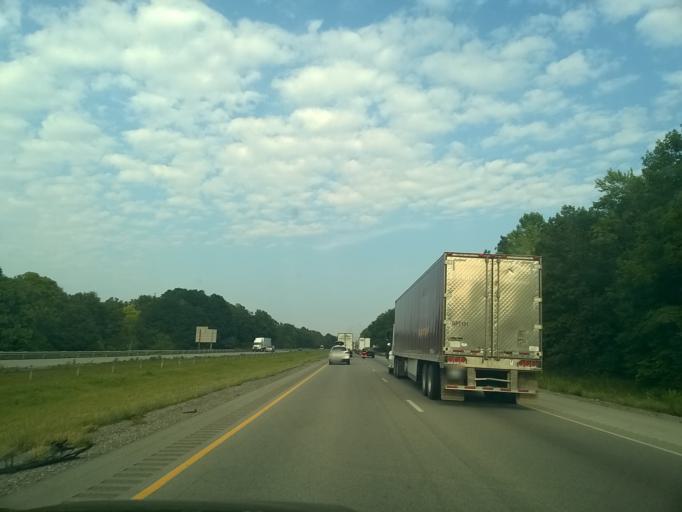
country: US
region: Indiana
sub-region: Putnam County
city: Cloverdale
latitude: 39.5310
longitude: -86.8604
